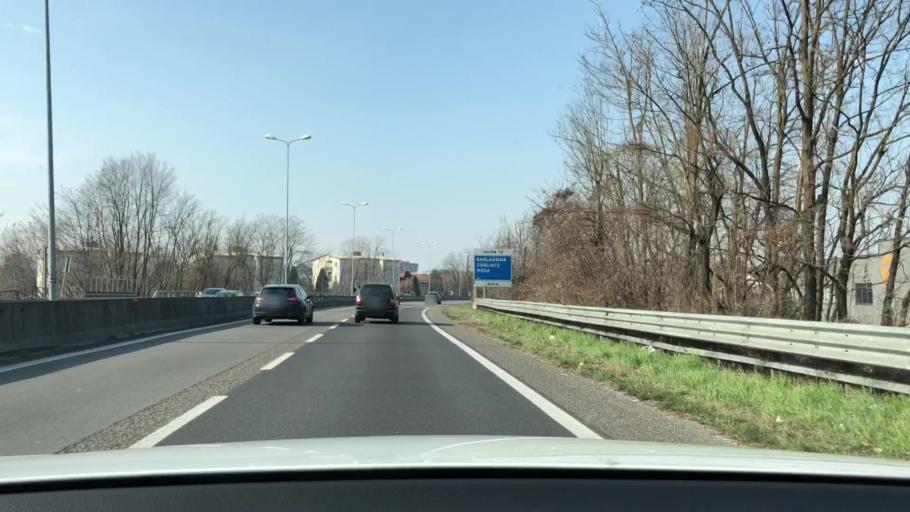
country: IT
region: Lombardy
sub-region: Provincia di Monza e Brianza
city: Barlassina
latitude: 45.6570
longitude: 9.1404
